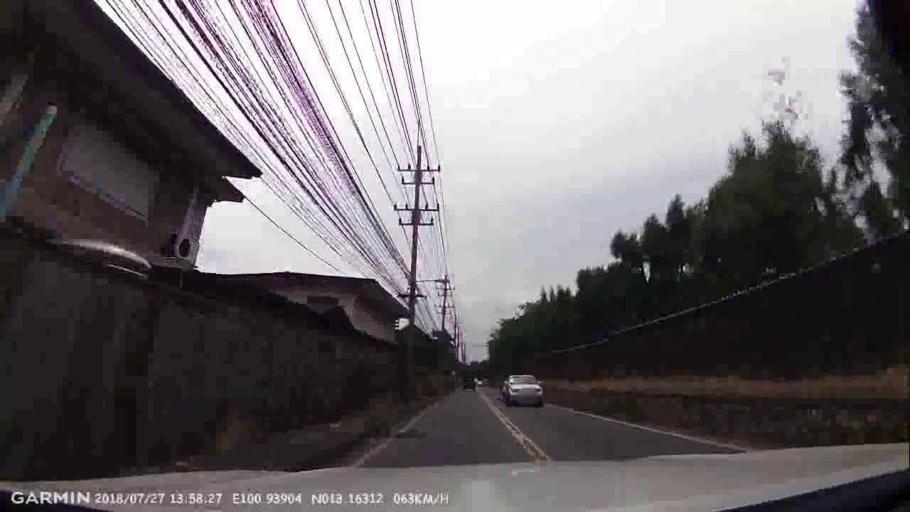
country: TH
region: Chon Buri
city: Si Racha
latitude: 13.1632
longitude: 100.9390
